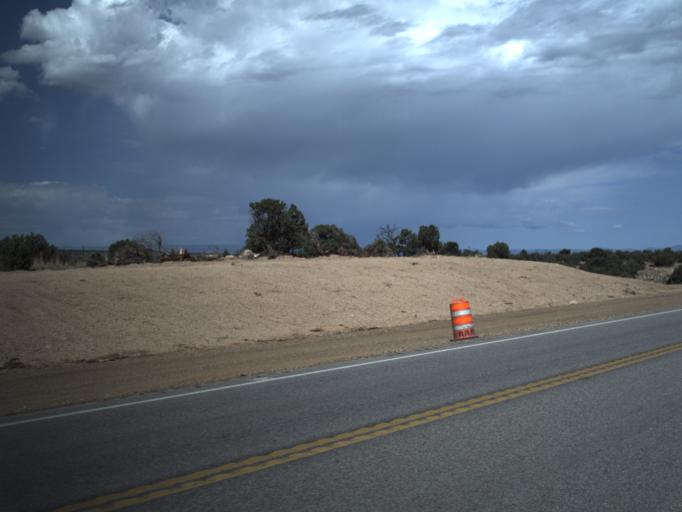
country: US
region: Utah
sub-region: Carbon County
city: East Carbon City
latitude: 39.4034
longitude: -110.4257
